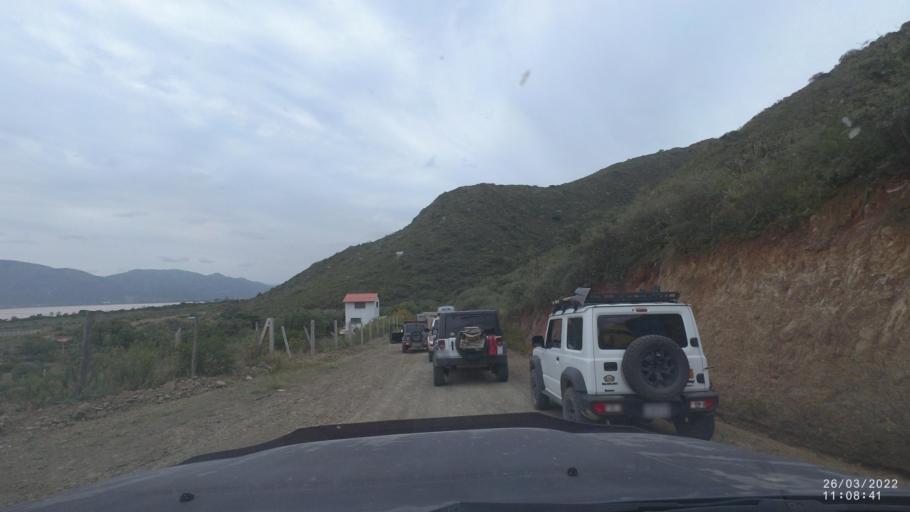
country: BO
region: Cochabamba
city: Tarata
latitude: -17.5342
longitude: -66.0209
